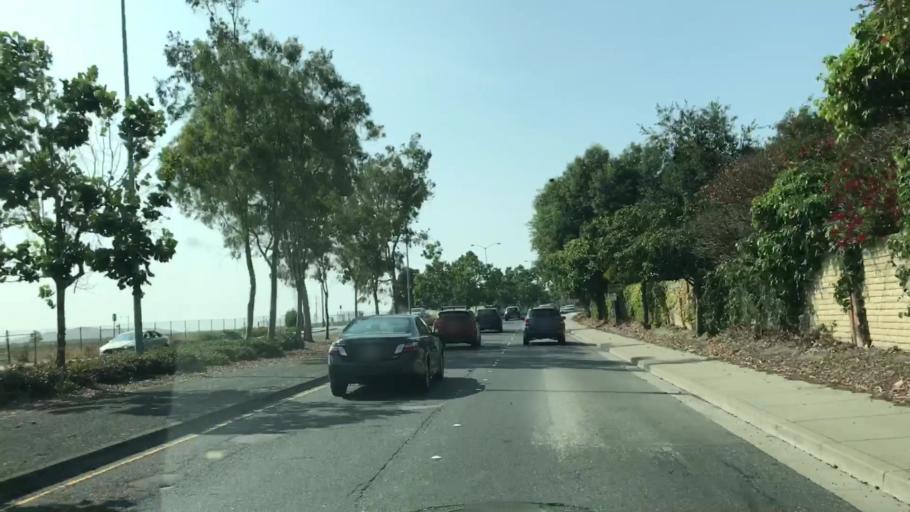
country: US
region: California
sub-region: Alameda County
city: Newark
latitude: 37.5695
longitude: -122.0749
